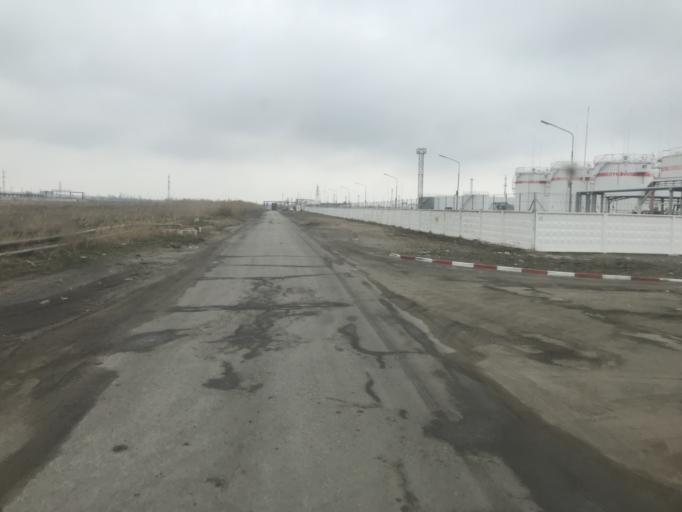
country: RU
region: Volgograd
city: Svetlyy Yar
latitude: 48.5102
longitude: 44.6392
